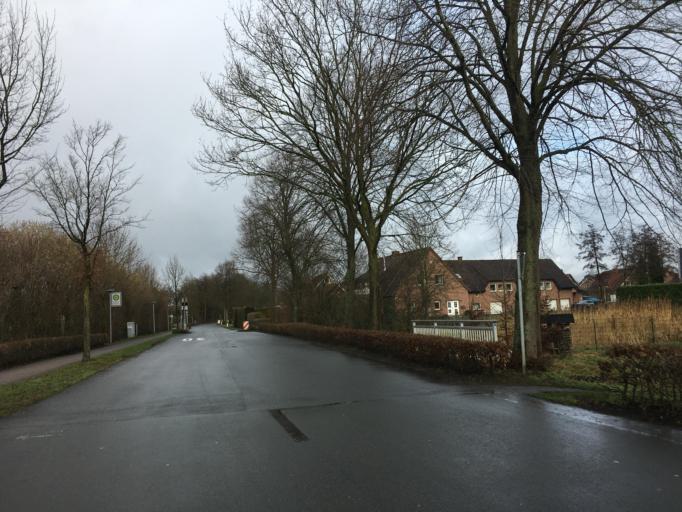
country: DE
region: North Rhine-Westphalia
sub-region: Regierungsbezirk Munster
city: Senden
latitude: 51.9188
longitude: 7.4744
